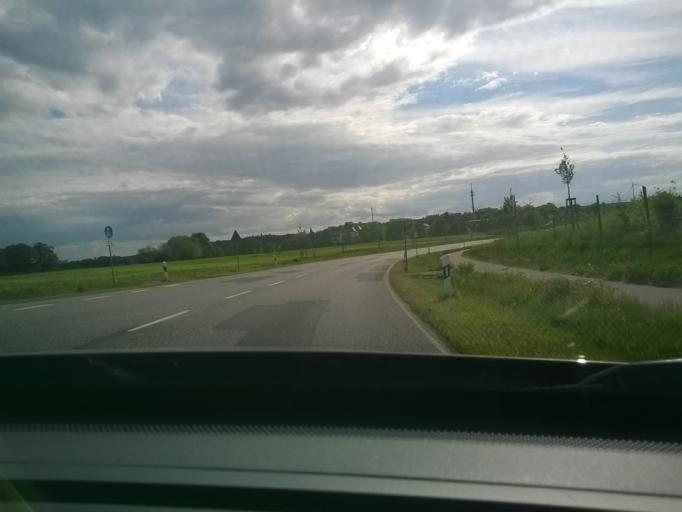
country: DE
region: Brandenburg
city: Wittstock
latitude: 53.1558
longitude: 12.4943
